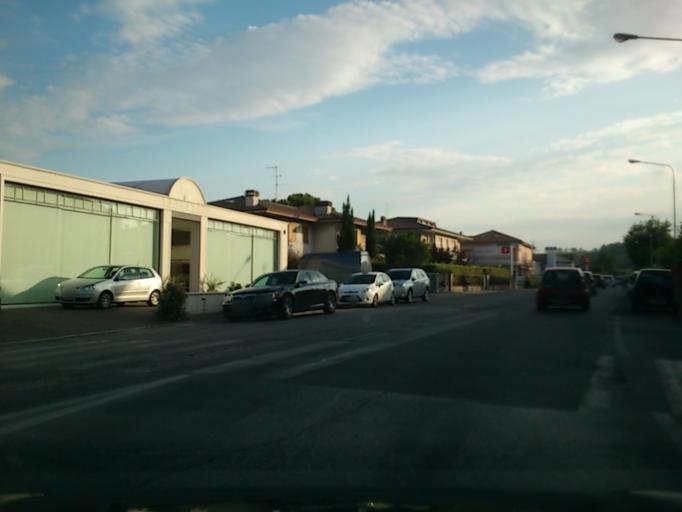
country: IT
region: The Marches
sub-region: Provincia di Pesaro e Urbino
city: Centinarola
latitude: 43.8317
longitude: 13.0005
